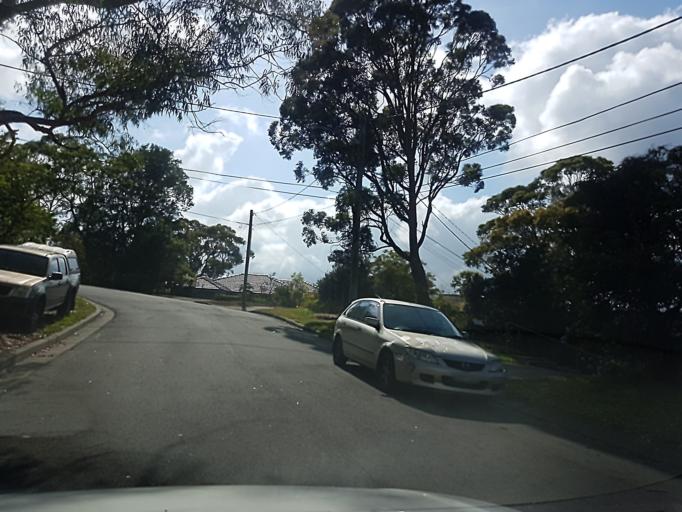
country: AU
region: New South Wales
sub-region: Warringah
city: Davidson
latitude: -33.7463
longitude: 151.2082
